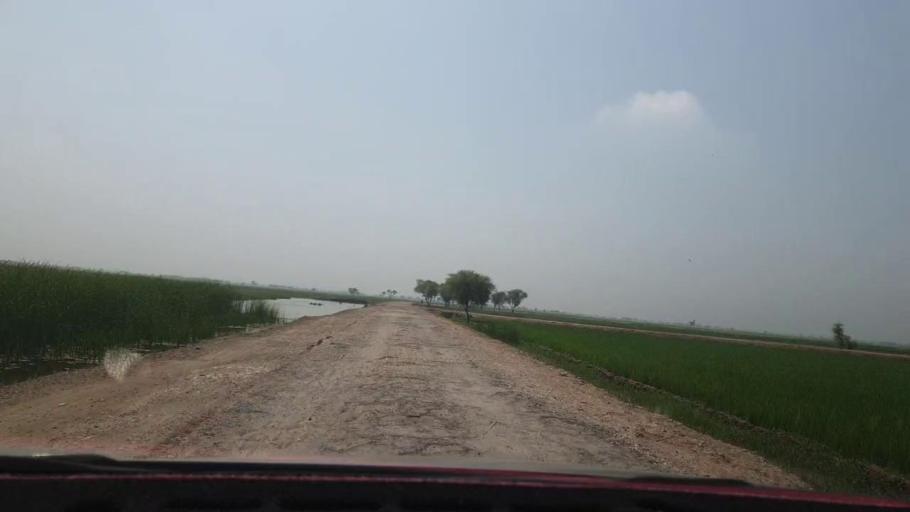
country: PK
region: Sindh
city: Nasirabad
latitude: 27.3995
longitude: 67.8493
